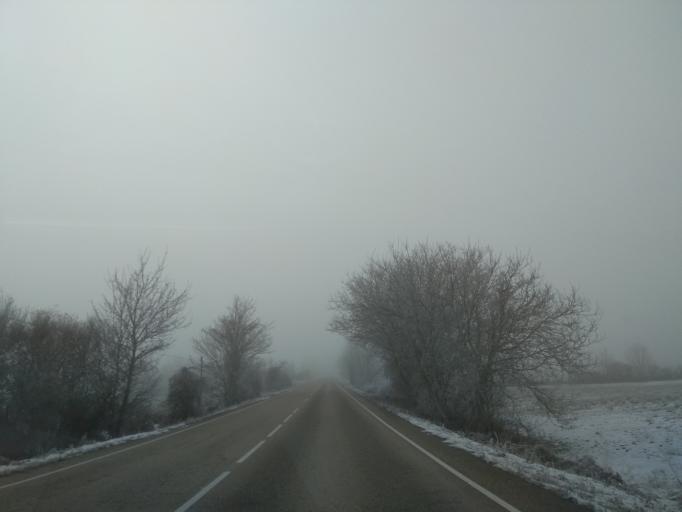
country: ES
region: Castille and Leon
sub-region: Provincia de Burgos
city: Espinosa de los Monteros
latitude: 43.0457
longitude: -3.4887
